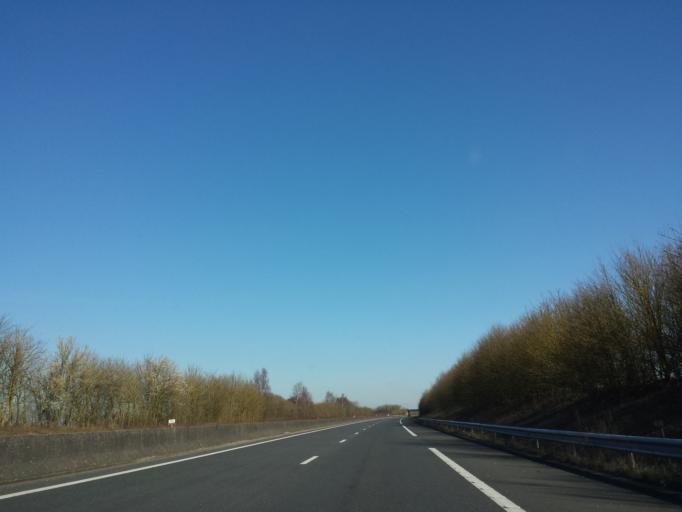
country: FR
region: Picardie
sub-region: Departement de l'Oise
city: Tille
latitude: 49.4947
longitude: 2.1689
